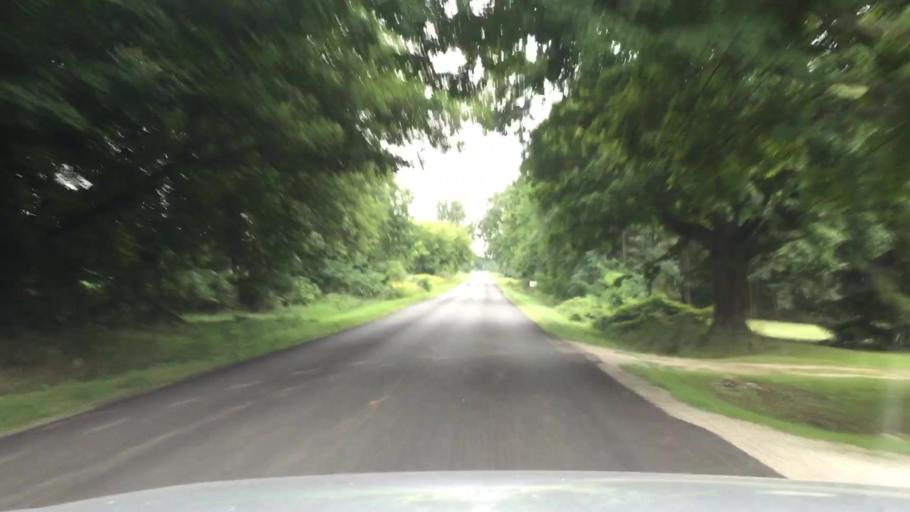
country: US
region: Michigan
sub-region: Shiawassee County
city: Durand
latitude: 42.8689
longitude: -84.0516
